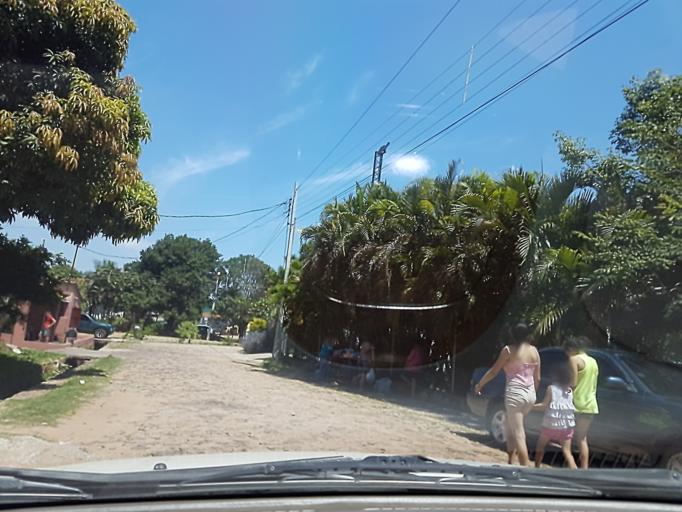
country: PY
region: Central
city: Fernando de la Mora
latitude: -25.2939
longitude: -57.5365
